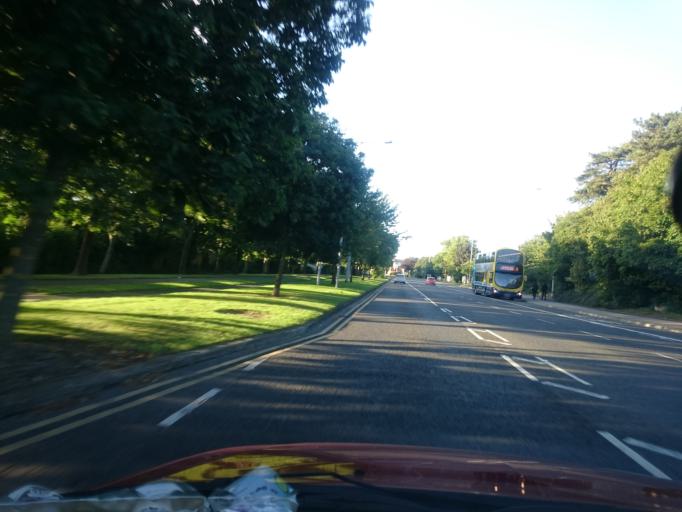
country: IE
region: Leinster
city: Sandyford
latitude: 53.2804
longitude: -6.2104
